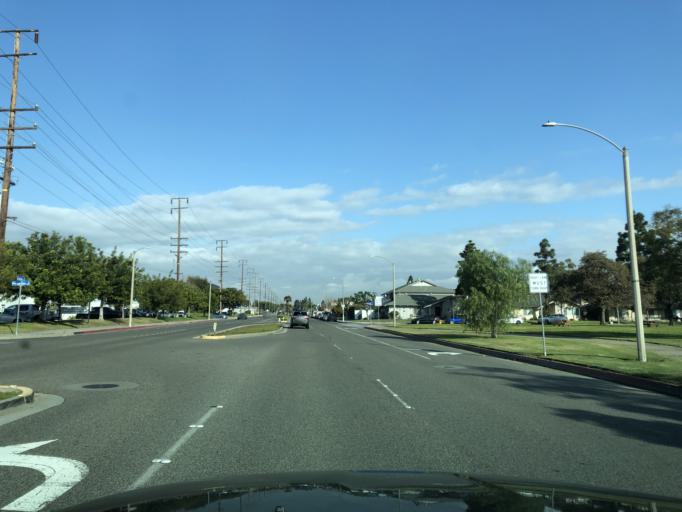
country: US
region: California
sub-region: Orange County
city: Westminster
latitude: 33.7315
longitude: -118.0326
